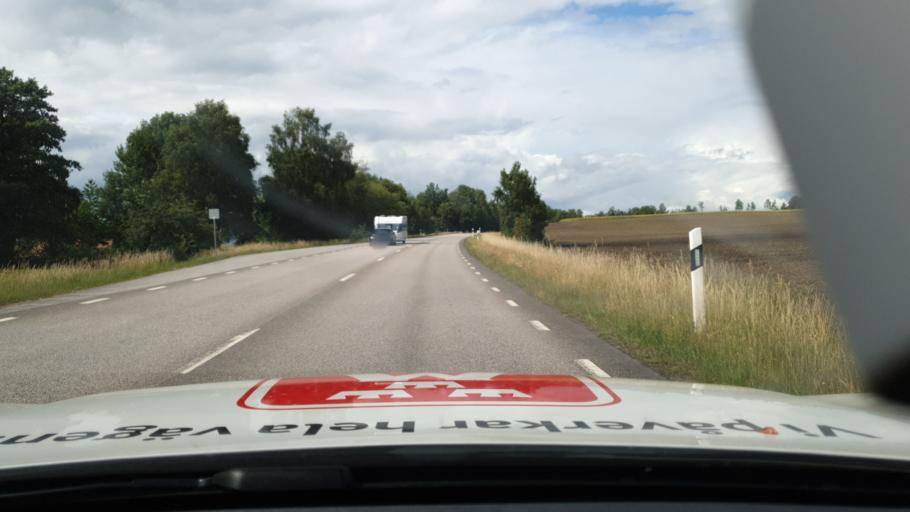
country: SE
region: Vaestra Goetaland
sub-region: Hjo Kommun
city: Hjo
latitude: 58.3239
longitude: 14.2623
